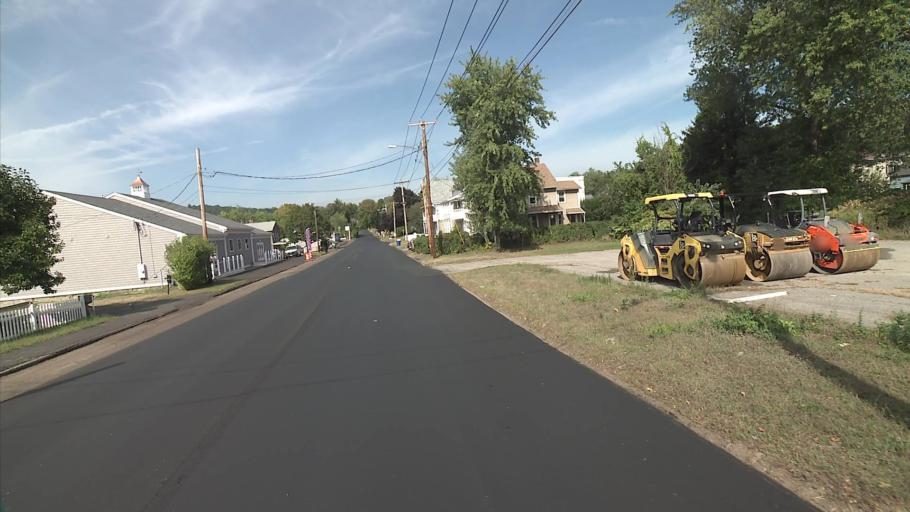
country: US
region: Connecticut
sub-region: Fairfield County
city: Shelton
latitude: 41.3285
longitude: -73.1047
